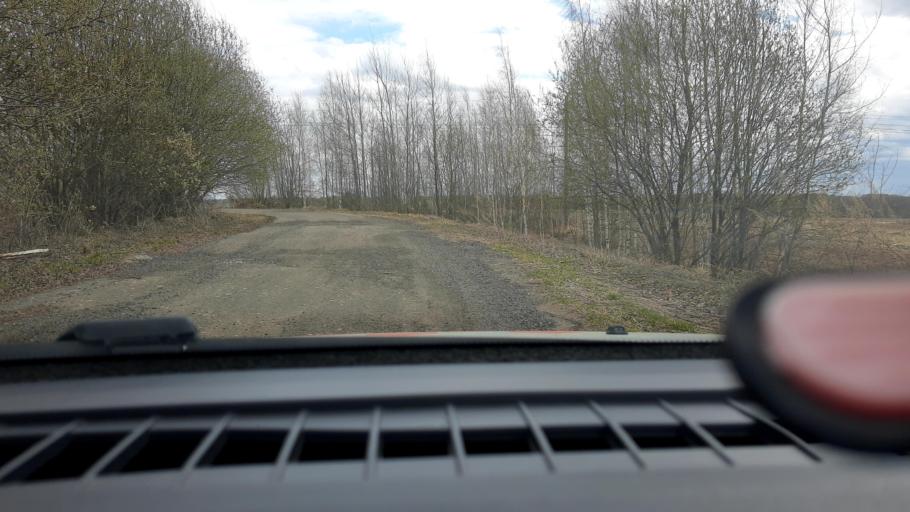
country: RU
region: Nizjnij Novgorod
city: Babino
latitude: 56.1659
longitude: 43.6814
